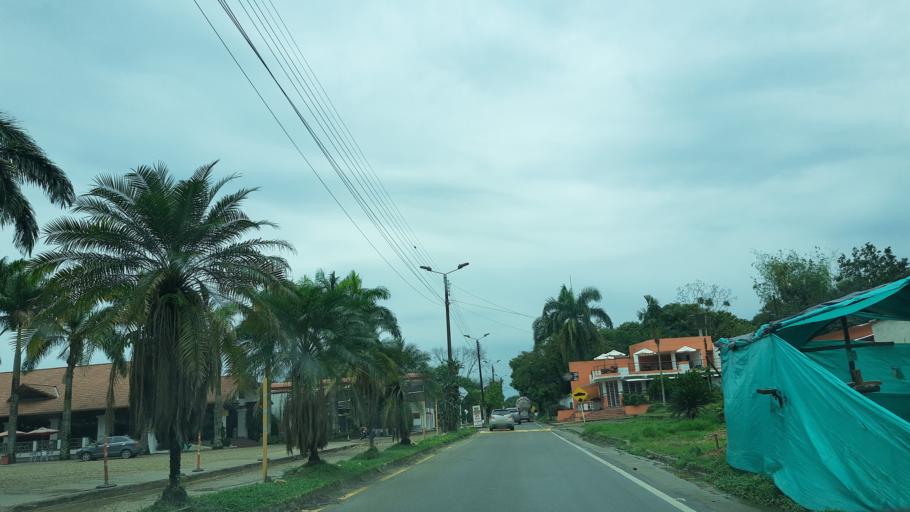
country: CO
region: Casanare
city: Monterrey
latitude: 4.8374
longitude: -72.9560
